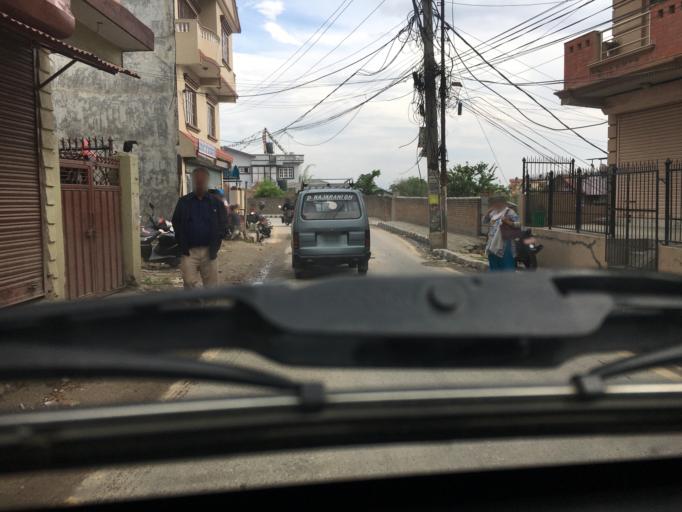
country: NP
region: Central Region
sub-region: Bagmati Zone
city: Kathmandu
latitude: 27.7429
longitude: 85.3474
